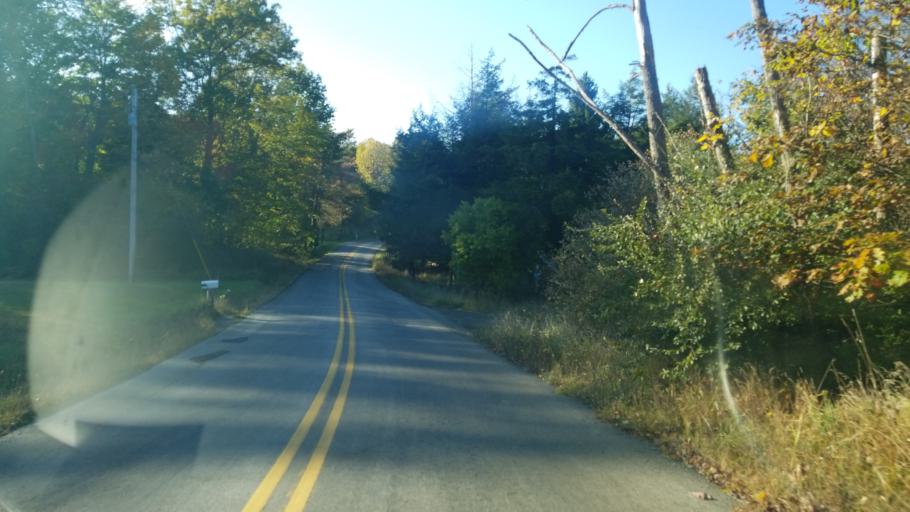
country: US
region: Pennsylvania
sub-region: Indiana County
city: Johnsonburg
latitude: 40.8979
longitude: -78.8934
